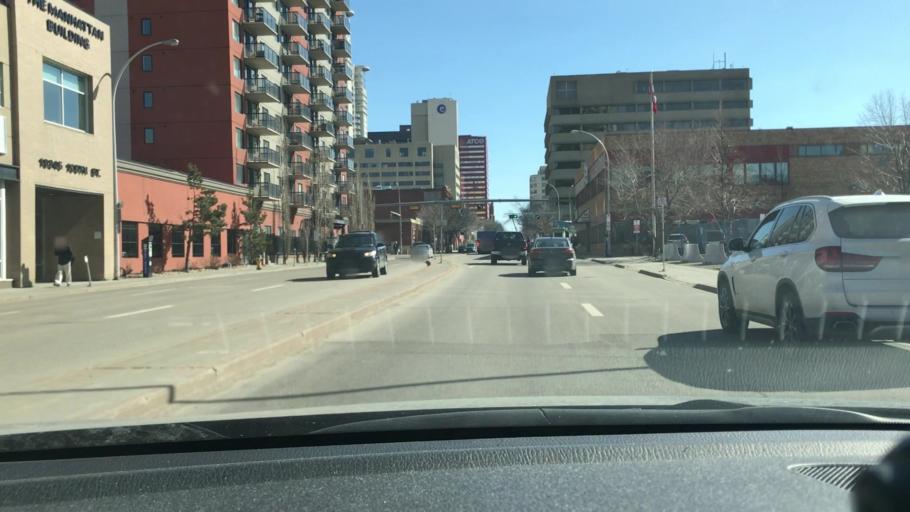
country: CA
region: Alberta
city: Edmonton
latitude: 53.5457
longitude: -113.5011
